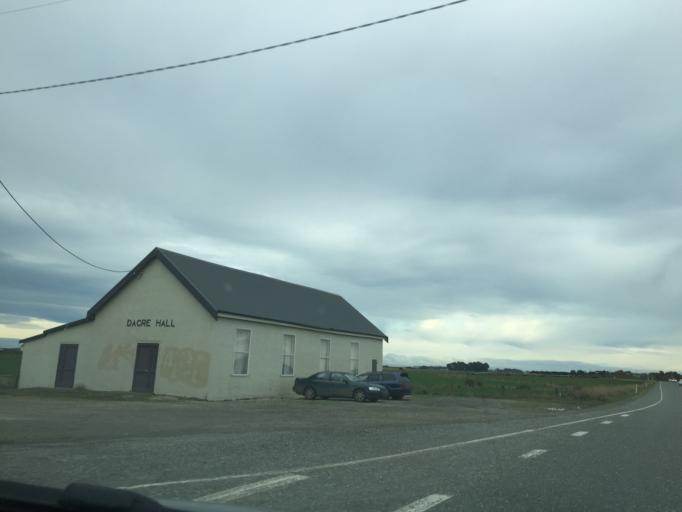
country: NZ
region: Southland
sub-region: Invercargill City
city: Invercargill
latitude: -46.3174
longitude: 168.6020
